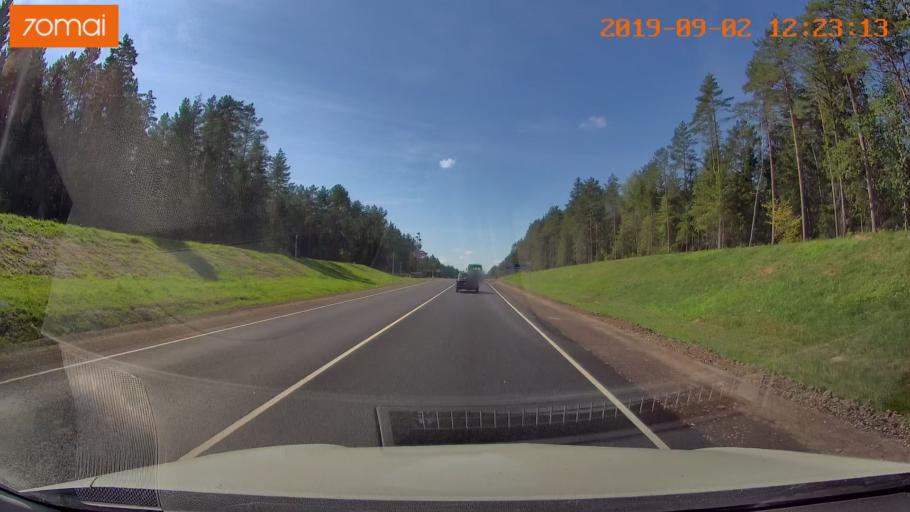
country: RU
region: Smolensk
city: Shumyachi
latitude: 53.8758
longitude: 32.6227
